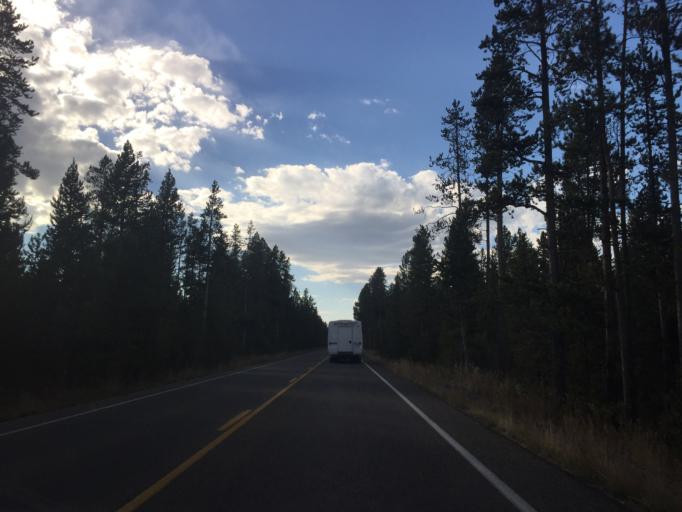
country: US
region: Montana
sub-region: Gallatin County
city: West Yellowstone
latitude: 44.6549
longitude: -111.0772
